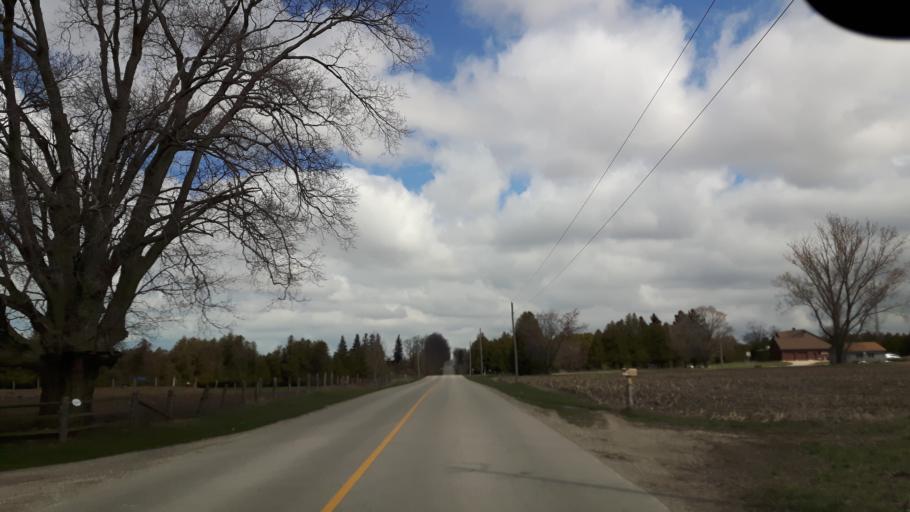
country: CA
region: Ontario
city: Goderich
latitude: 43.6649
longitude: -81.6846
